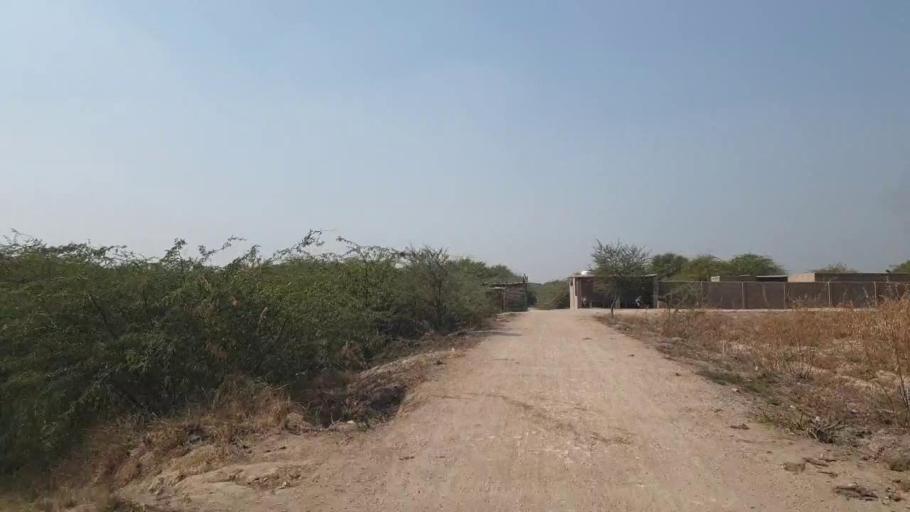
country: PK
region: Sindh
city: Chambar
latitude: 25.4109
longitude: 68.9080
